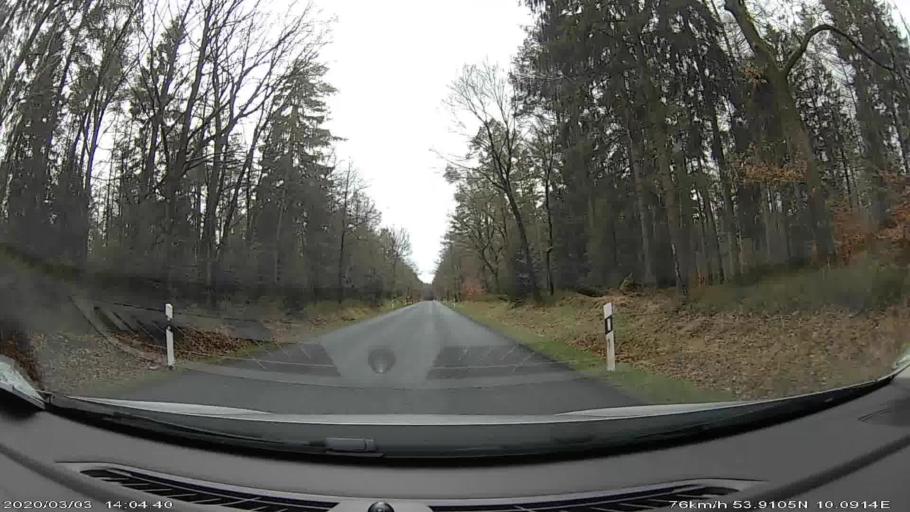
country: DE
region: Schleswig-Holstein
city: Hartenholm
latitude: 53.9098
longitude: 10.0909
